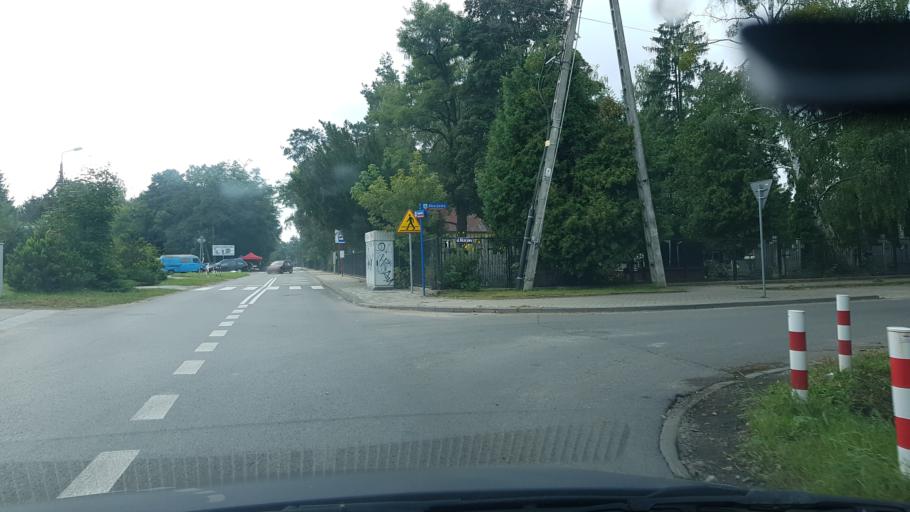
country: PL
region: Masovian Voivodeship
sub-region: Powiat piaseczynski
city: Konstancin-Jeziorna
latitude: 52.0682
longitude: 21.0998
